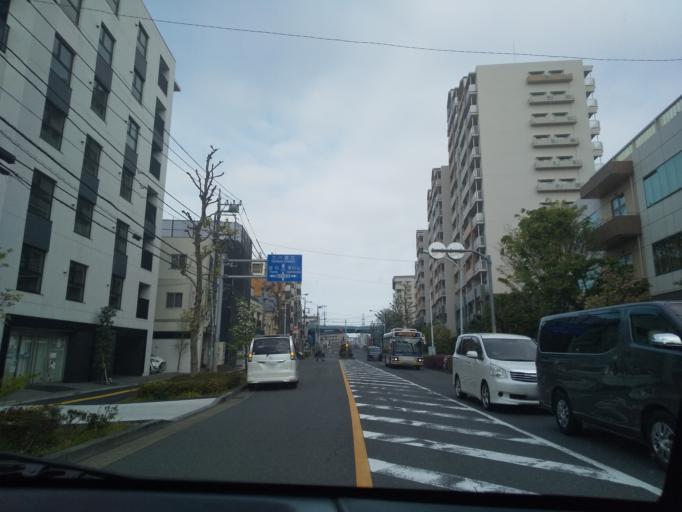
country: JP
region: Tokyo
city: Kokubunji
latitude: 35.6960
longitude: 139.4688
